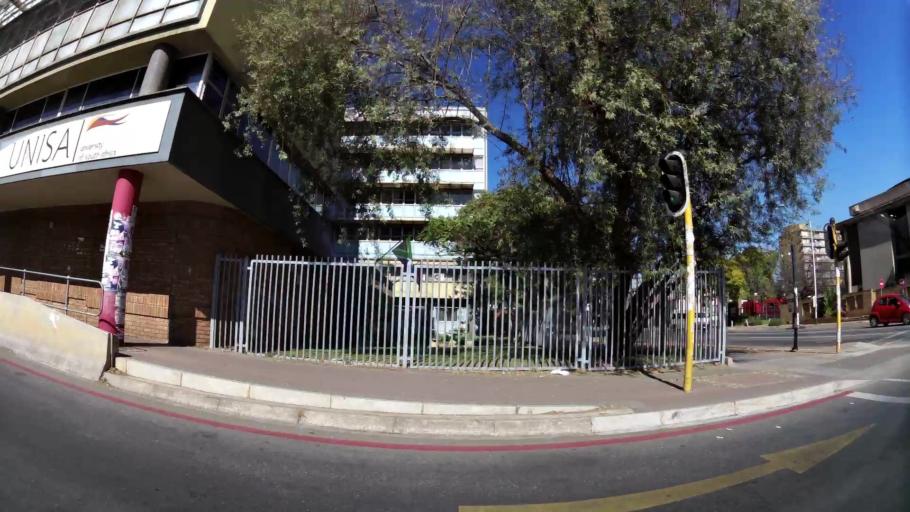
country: ZA
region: Gauteng
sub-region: City of Tshwane Metropolitan Municipality
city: Pretoria
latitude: -25.7507
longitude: 28.1935
